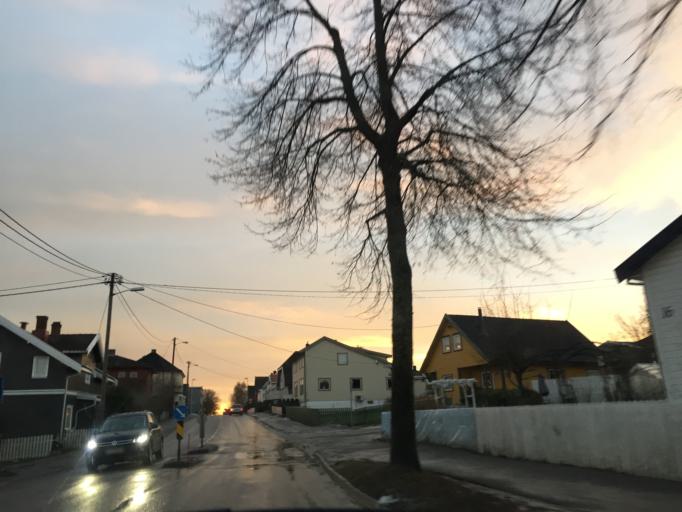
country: NO
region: Ostfold
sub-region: Moss
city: Moss
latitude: 59.4356
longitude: 10.6425
